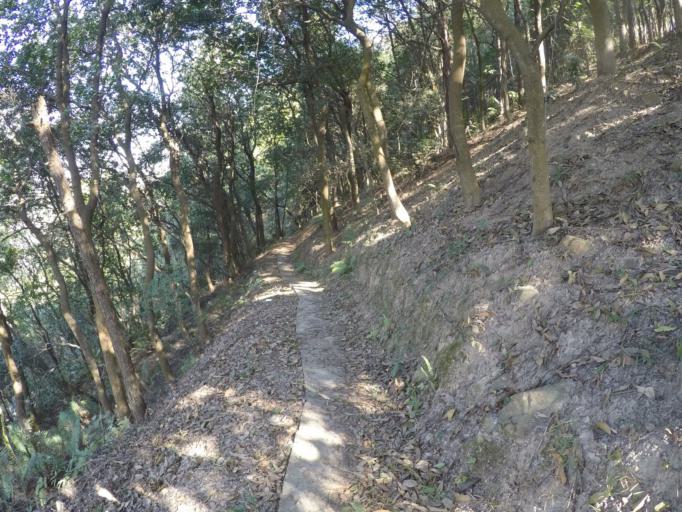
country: CN
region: Guangdong
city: Huancheng
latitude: 22.4652
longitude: 113.4082
